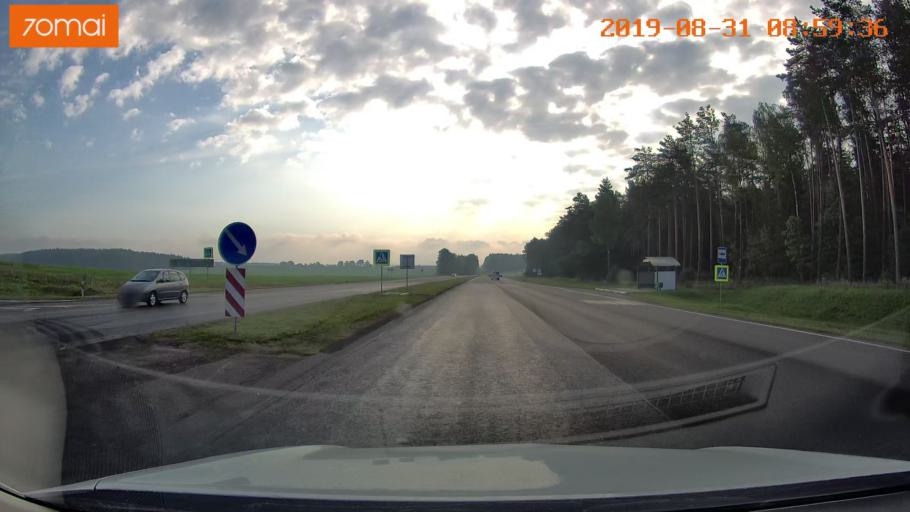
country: BY
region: Minsk
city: Smilavichy
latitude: 53.7642
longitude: 28.2130
